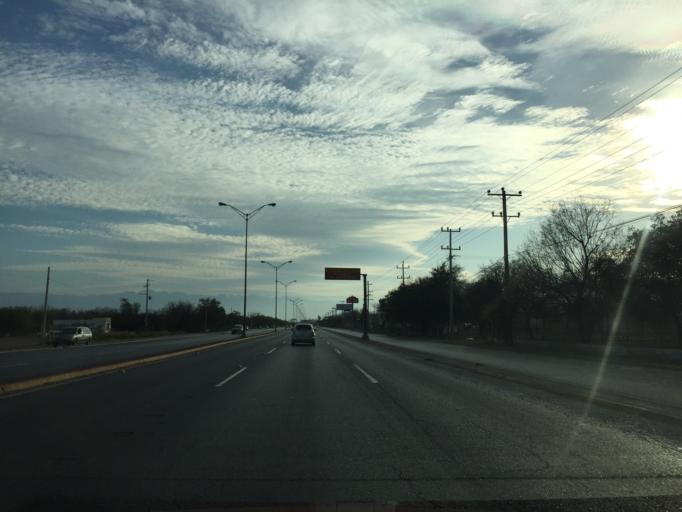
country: MX
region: Nuevo Leon
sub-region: Apodaca
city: Fraccionamiento Cosmopolis Octavo Sector
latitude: 25.8183
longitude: -100.2667
